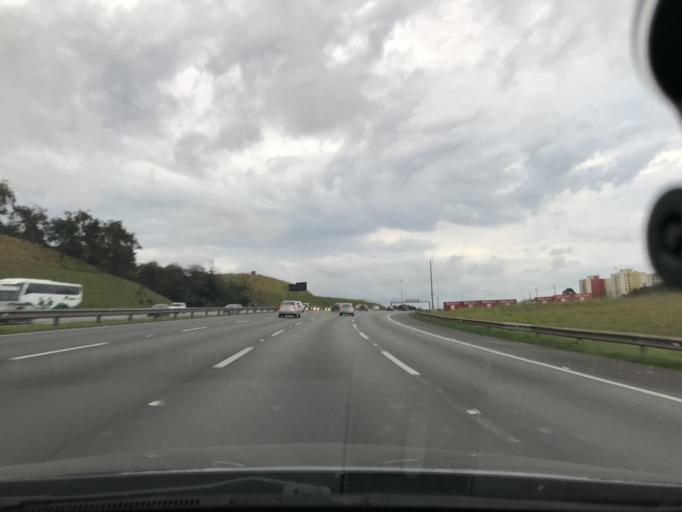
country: BR
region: Sao Paulo
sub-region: Osasco
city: Osasco
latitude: -23.5649
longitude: -46.8196
